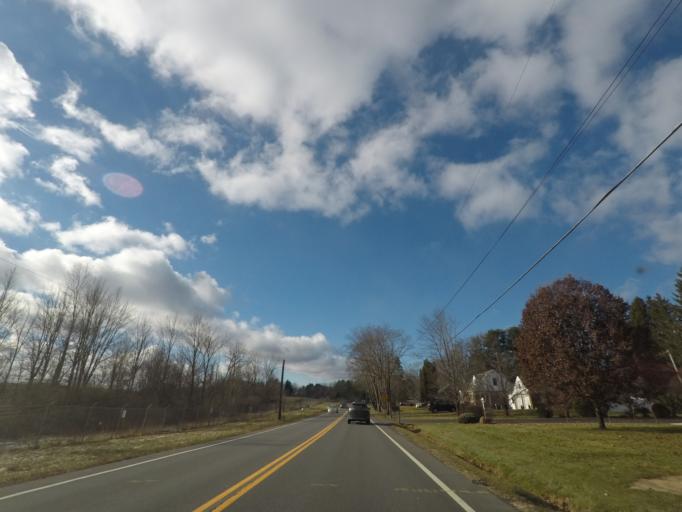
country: US
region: New York
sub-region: Schenectady County
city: East Glenville
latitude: 42.8676
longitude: -73.9192
